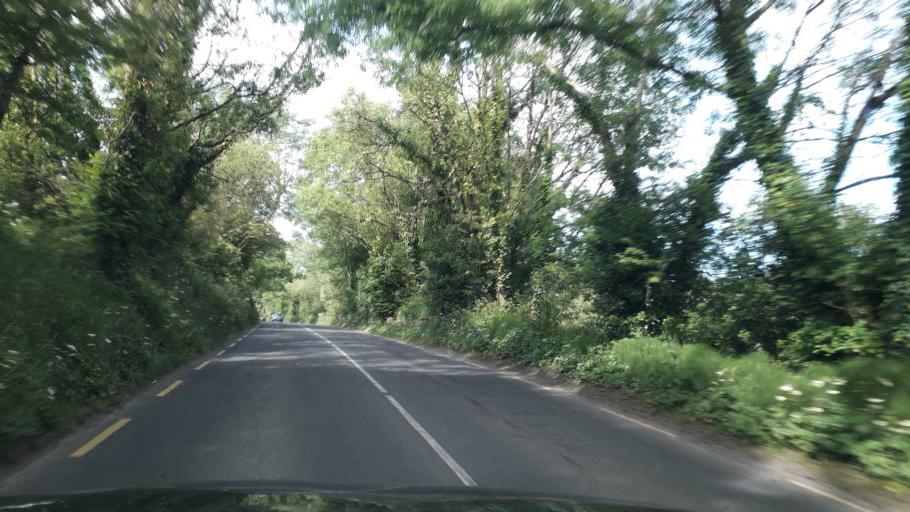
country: IE
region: Leinster
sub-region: Loch Garman
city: Castlebridge
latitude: 52.4110
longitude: -6.4234
